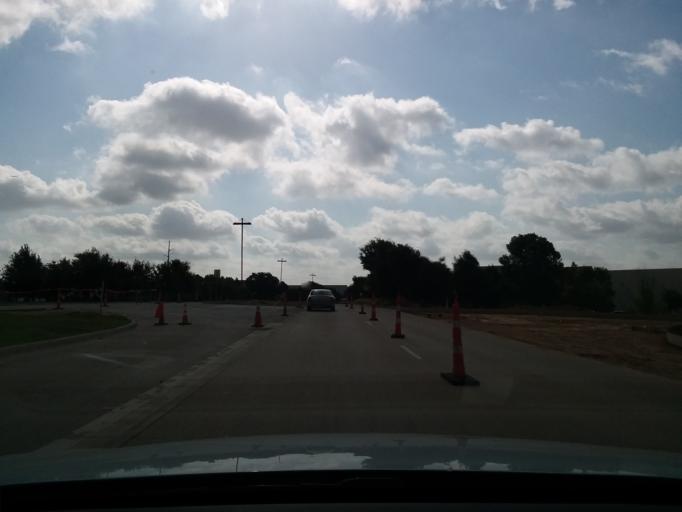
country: US
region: Texas
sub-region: Dallas County
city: Coppell
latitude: 32.9947
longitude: -97.0424
